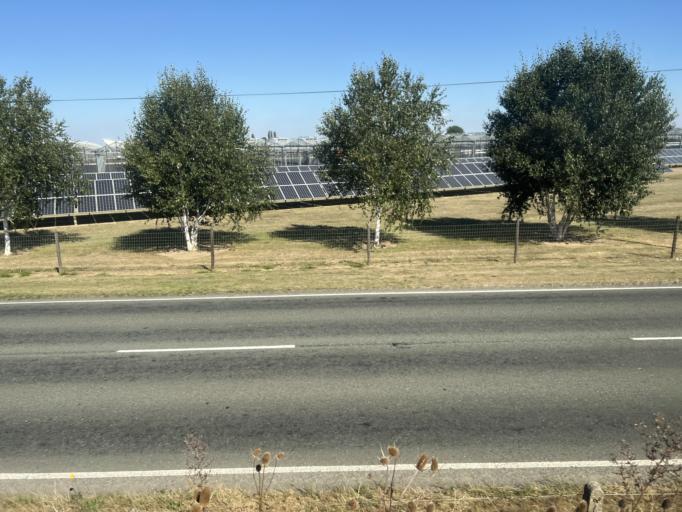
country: GB
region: England
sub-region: Lincolnshire
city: Donington
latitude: 52.9748
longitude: -0.1468
